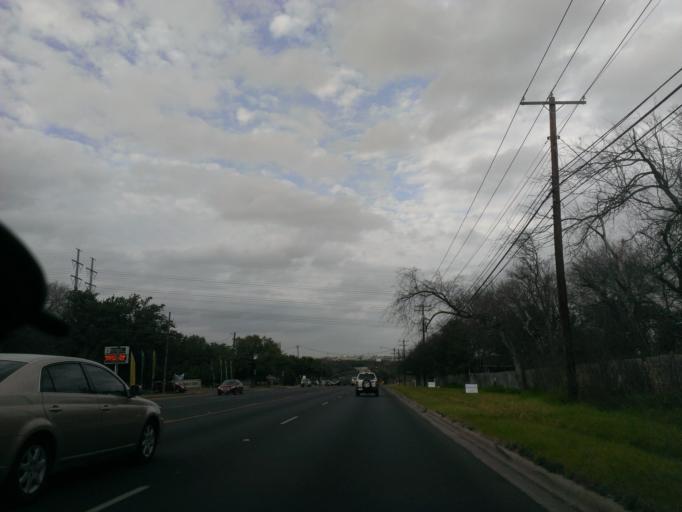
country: US
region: Texas
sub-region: Travis County
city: Wells Branch
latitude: 30.3898
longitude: -97.6827
